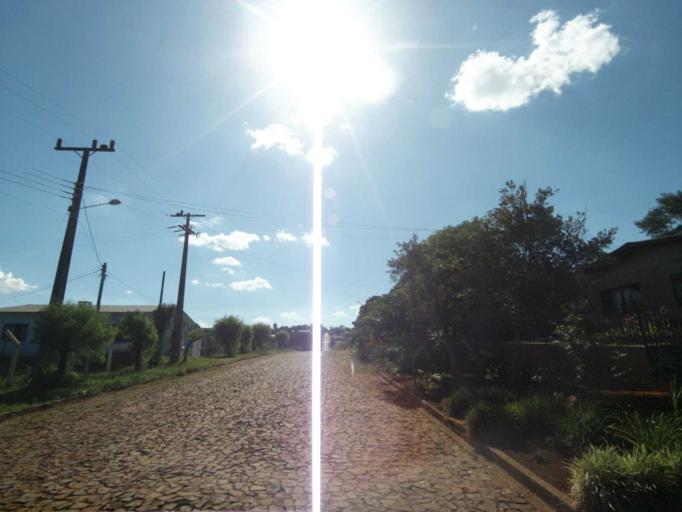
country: BR
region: Parana
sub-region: Laranjeiras Do Sul
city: Laranjeiras do Sul
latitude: -25.3835
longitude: -52.1987
